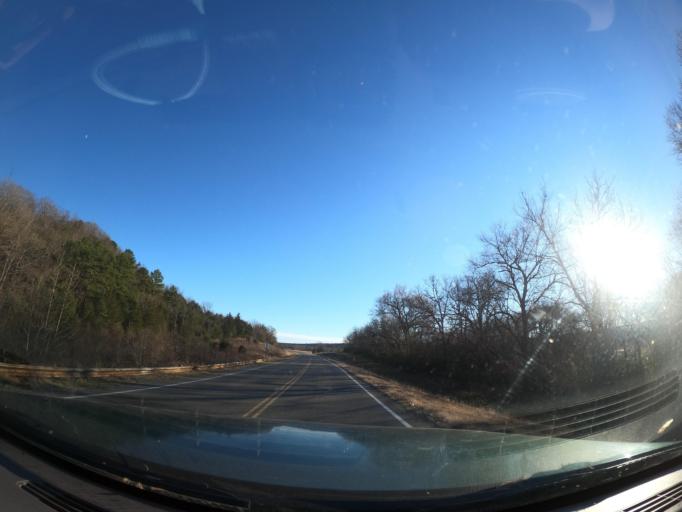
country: US
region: Oklahoma
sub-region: Latimer County
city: Wilburton
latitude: 34.9378
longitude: -95.3411
